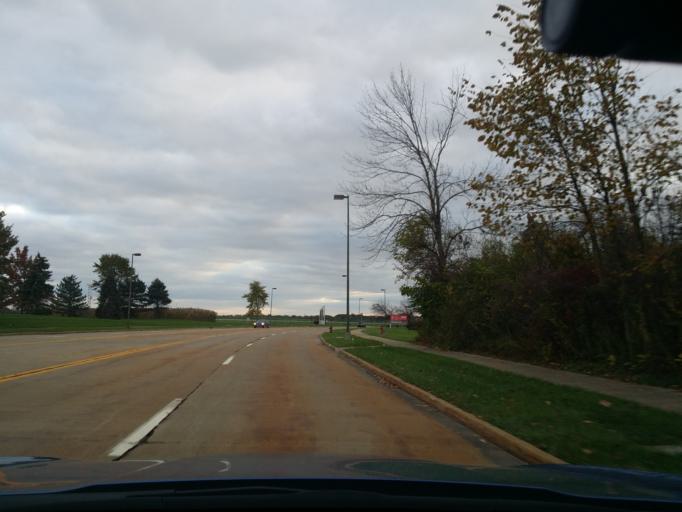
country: US
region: Ohio
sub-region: Cuyahoga County
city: Fairview Park
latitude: 41.4047
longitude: -81.8724
